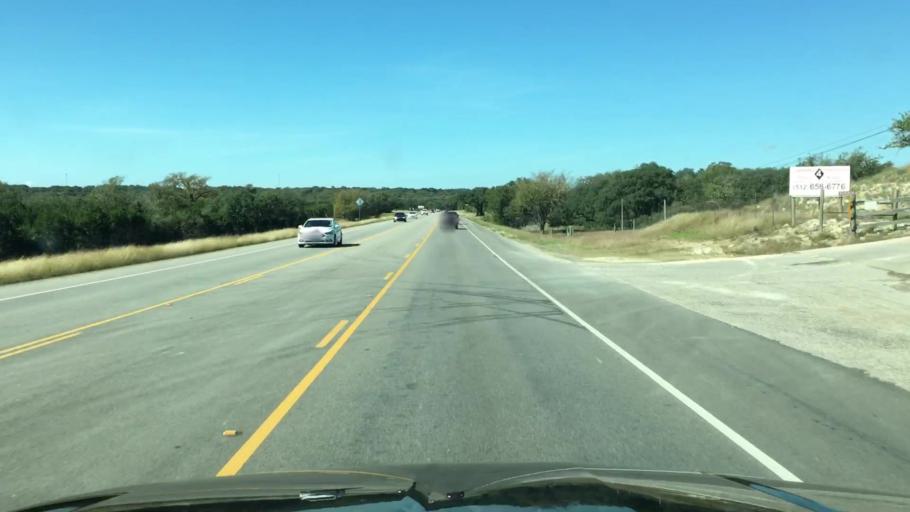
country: US
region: Texas
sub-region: Hays County
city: Dripping Springs
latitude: 30.2005
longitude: -98.1903
